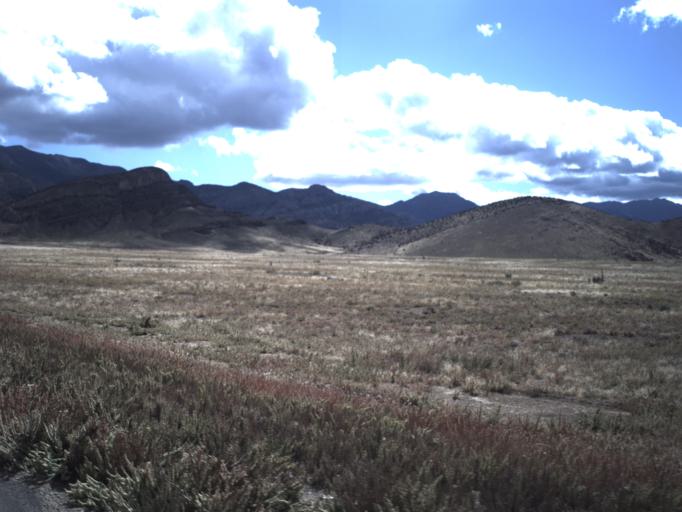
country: US
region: Utah
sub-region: Beaver County
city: Milford
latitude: 38.5070
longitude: -113.6135
